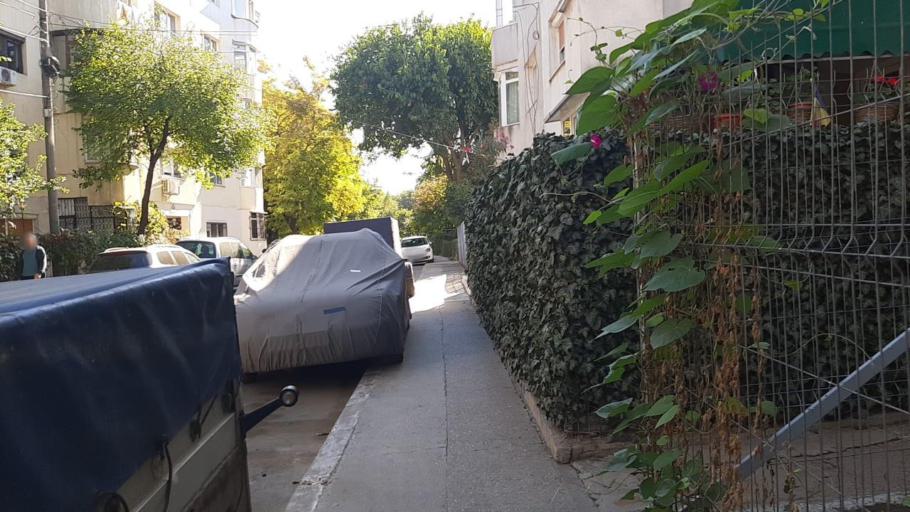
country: RO
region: Galati
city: Galati
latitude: 45.4427
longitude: 28.0246
